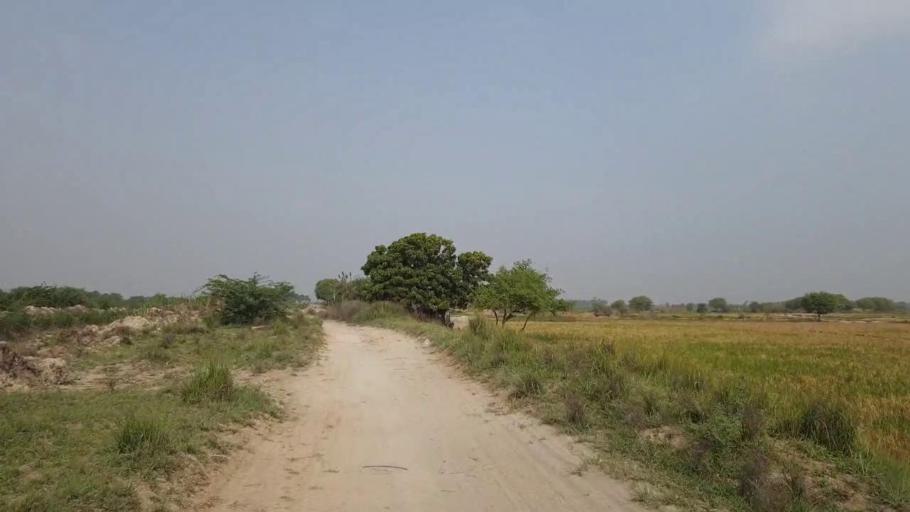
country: PK
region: Sindh
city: Kario
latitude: 24.7671
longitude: 68.5236
